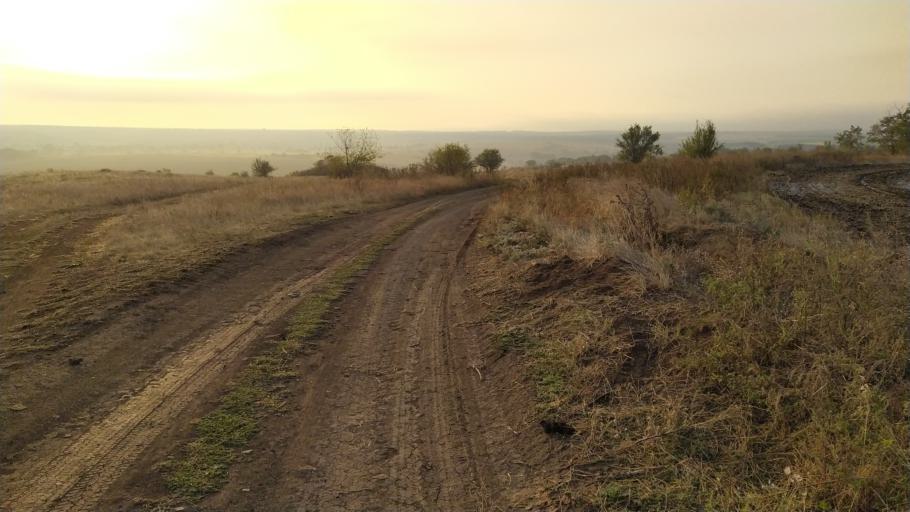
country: RU
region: Rostov
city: Gornyy
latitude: 47.8907
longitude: 40.2406
